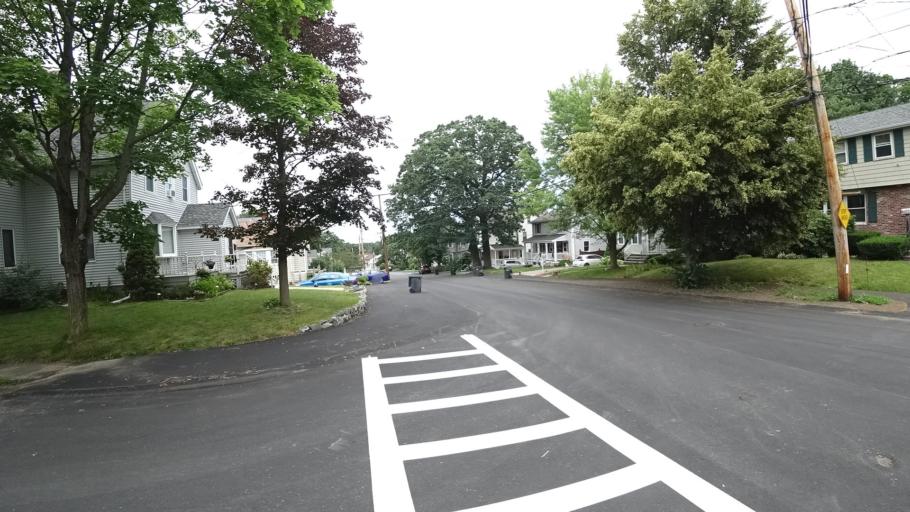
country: US
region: Massachusetts
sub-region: Norfolk County
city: Dedham
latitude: 42.2381
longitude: -71.1497
